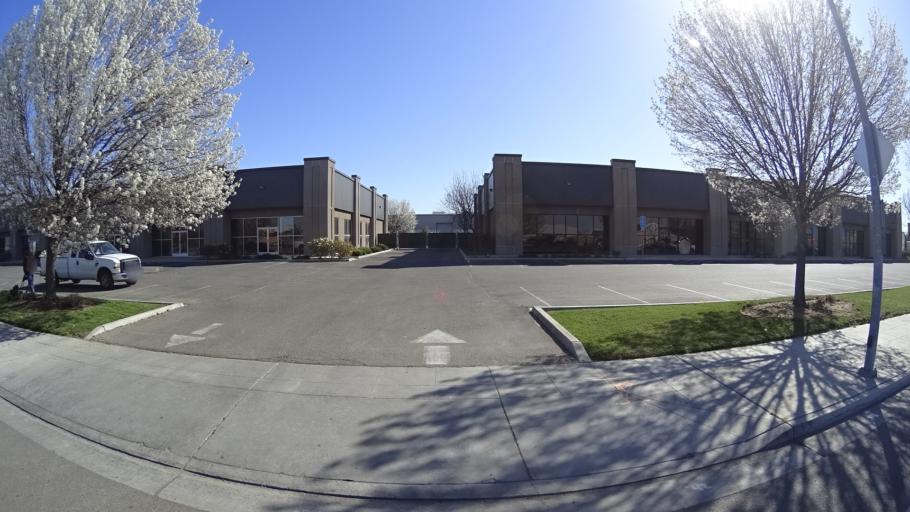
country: US
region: California
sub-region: Fresno County
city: West Park
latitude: 36.8002
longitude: -119.8624
